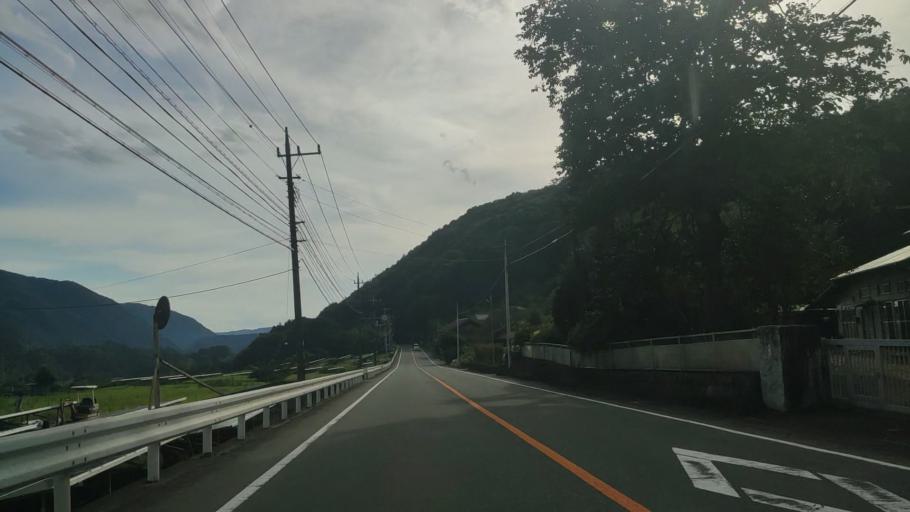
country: JP
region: Gunma
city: Omamacho-omama
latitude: 36.5311
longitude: 139.3246
